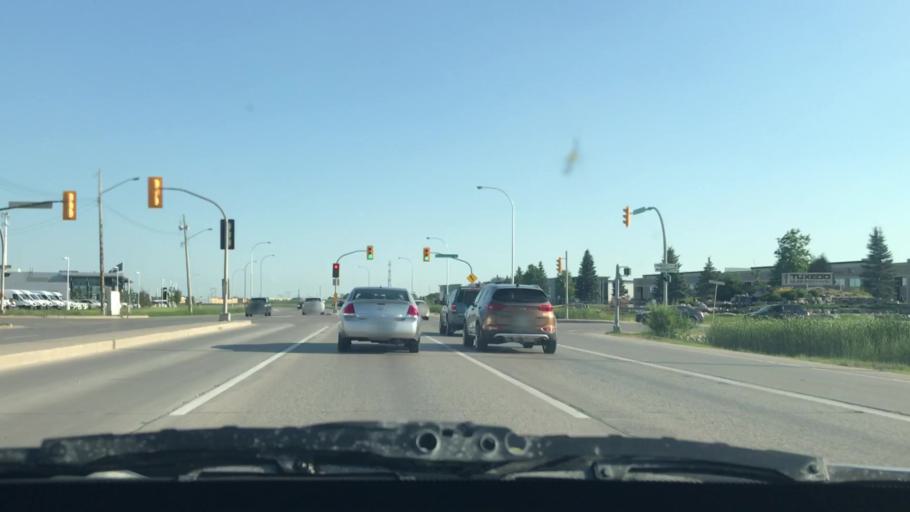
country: CA
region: Manitoba
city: Winnipeg
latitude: 49.8327
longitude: -97.2097
